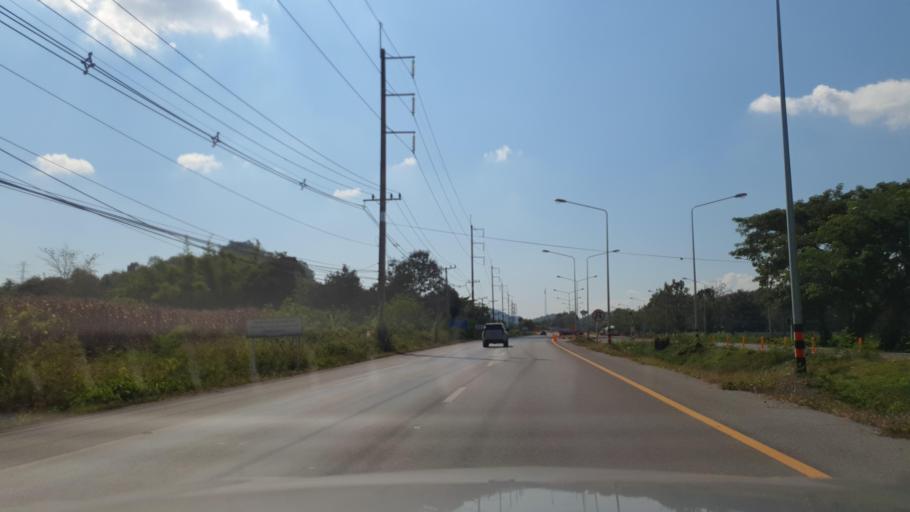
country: TH
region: Nan
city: Nan
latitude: 18.8926
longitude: 100.7538
